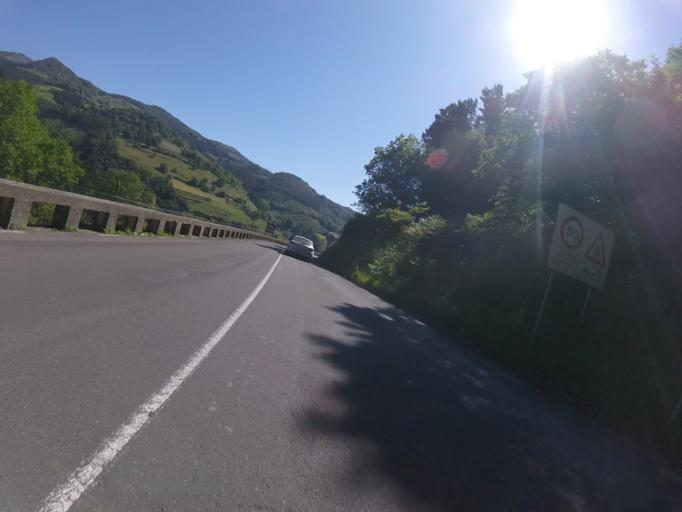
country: ES
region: Basque Country
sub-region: Provincia de Guipuzcoa
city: Albiztur
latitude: 43.1272
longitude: -2.1344
